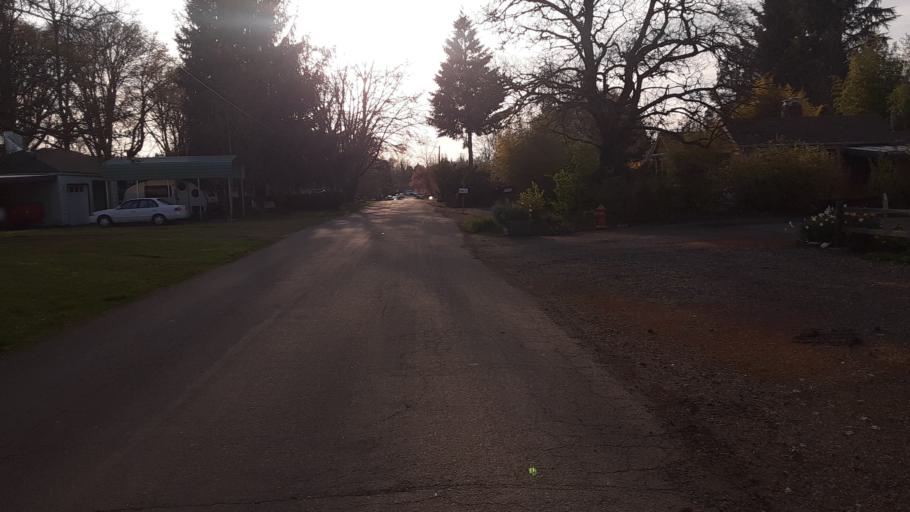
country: US
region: Oregon
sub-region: Benton County
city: Corvallis
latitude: 44.5494
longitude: -123.2601
